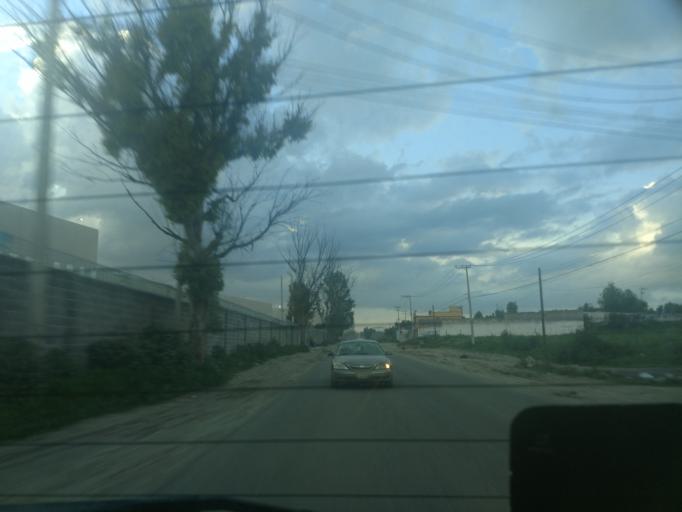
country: MX
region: Mexico
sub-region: Cuautitlan
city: Barrio Tlatenco
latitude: 19.7434
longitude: -99.1996
